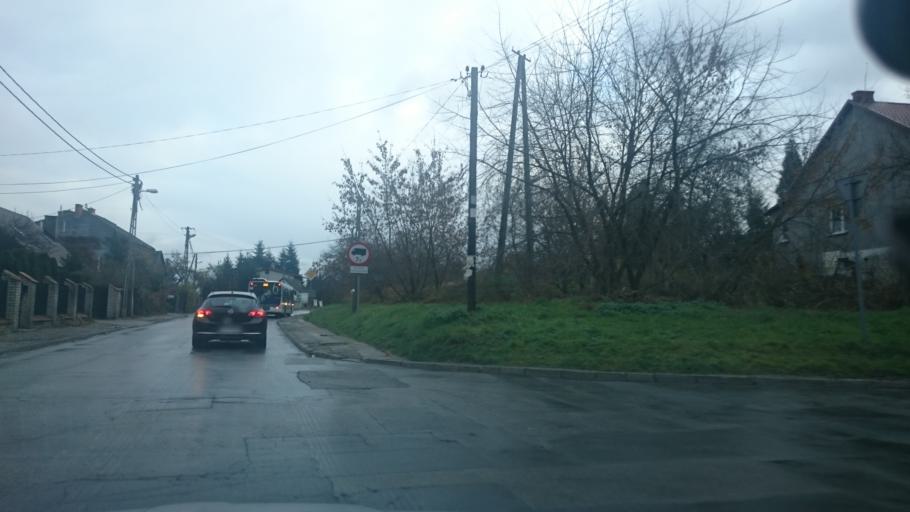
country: PL
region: Lesser Poland Voivodeship
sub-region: Powiat wielicki
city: Czarnochowice
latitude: 50.0231
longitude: 19.9996
